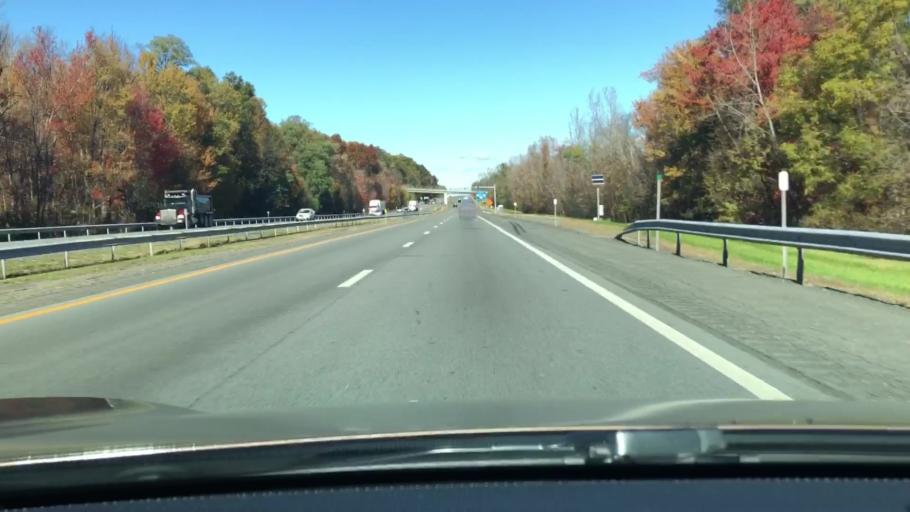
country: US
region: New York
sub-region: Orange County
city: Firthcliffe
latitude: 41.4252
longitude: -74.0684
